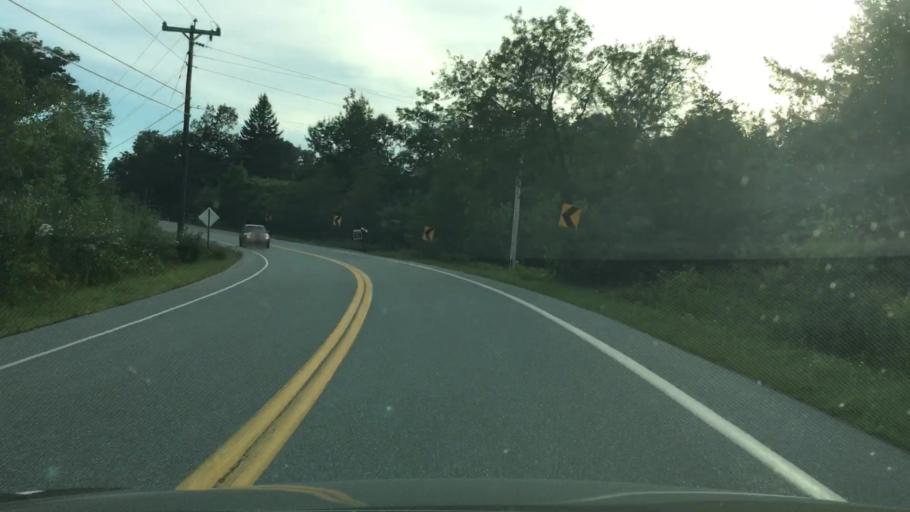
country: US
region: Maine
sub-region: Hancock County
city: Castine
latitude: 44.4468
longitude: -68.7851
